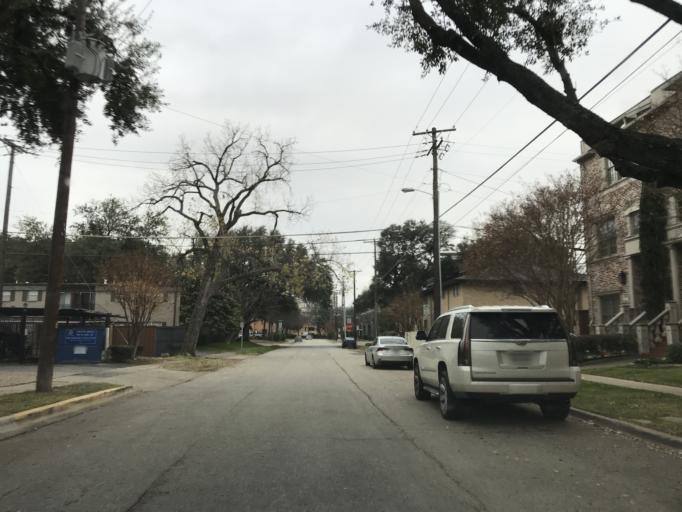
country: US
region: Texas
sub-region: Dallas County
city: Highland Park
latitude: 32.8184
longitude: -96.8046
